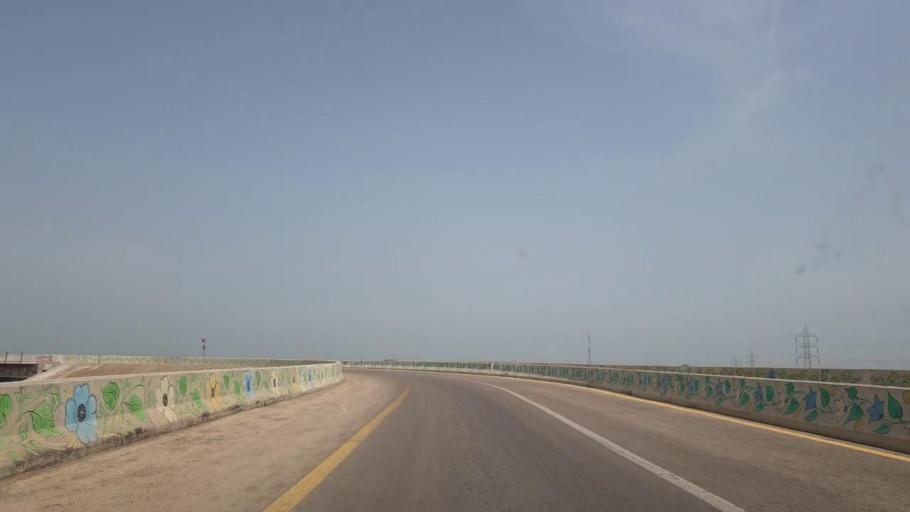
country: PK
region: Sindh
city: Sakrand
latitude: 26.1550
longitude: 68.2490
